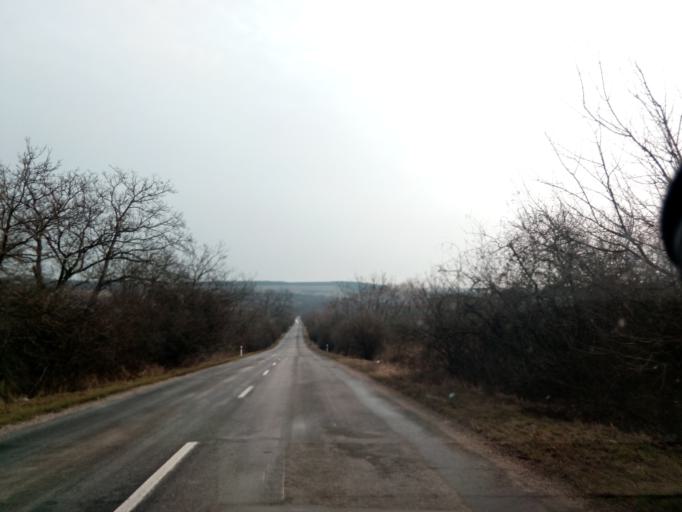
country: SK
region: Kosicky
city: Secovce
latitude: 48.6358
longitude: 21.4942
